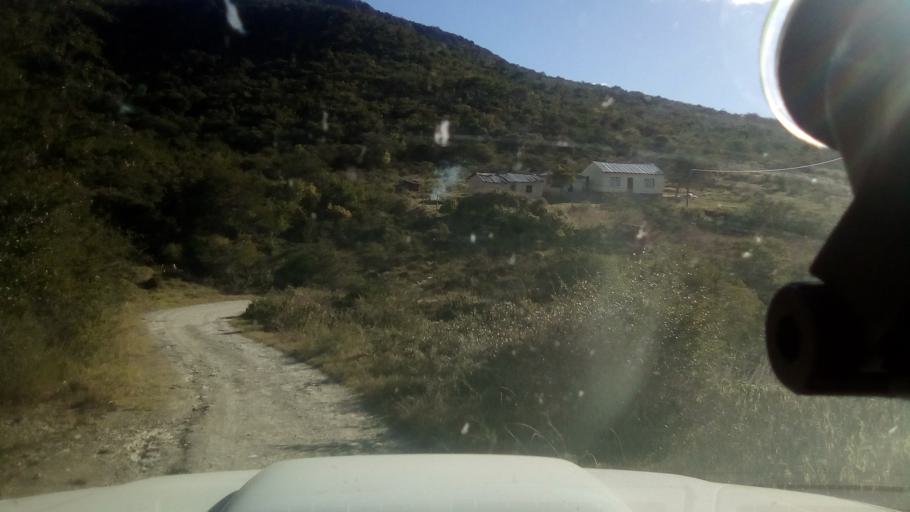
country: ZA
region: Eastern Cape
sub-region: Buffalo City Metropolitan Municipality
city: Bhisho
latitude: -32.7328
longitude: 27.3473
